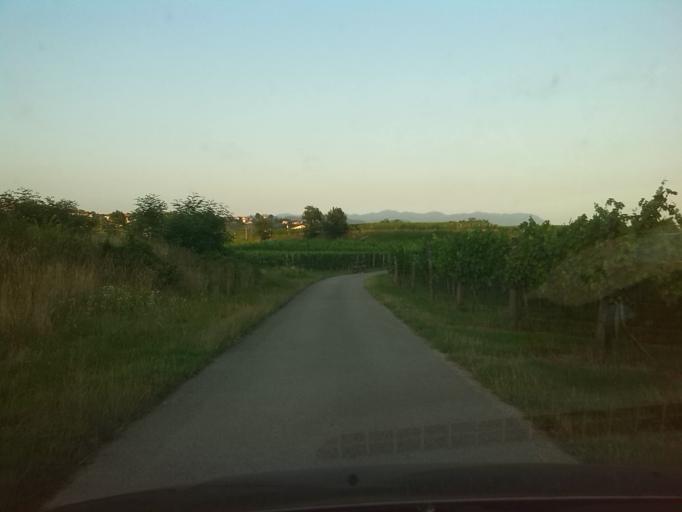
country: IT
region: Friuli Venezia Giulia
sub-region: Provincia di Gorizia
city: Cormons
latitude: 45.9775
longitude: 13.4911
